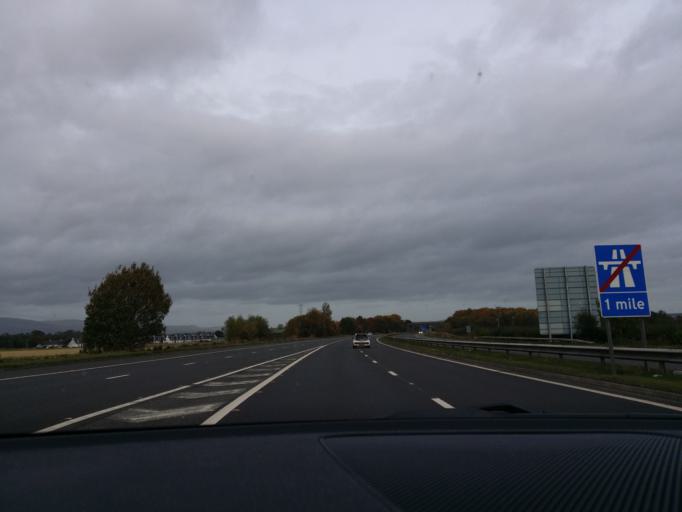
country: GB
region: Scotland
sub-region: Falkirk
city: Airth
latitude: 56.0472
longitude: -3.7788
